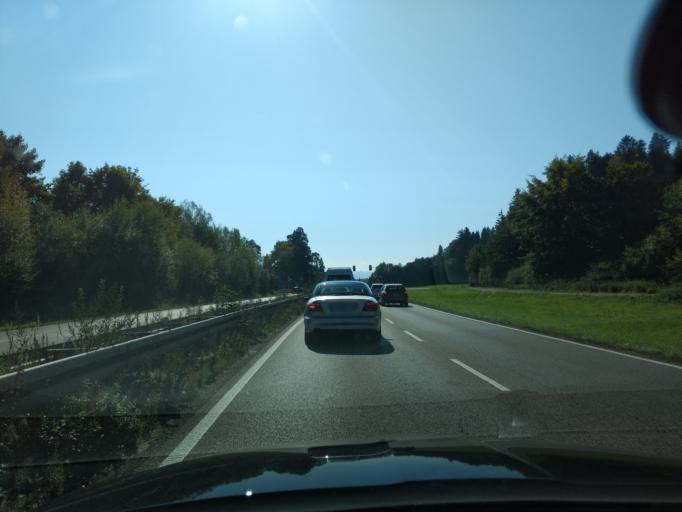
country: DE
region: Bavaria
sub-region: Upper Bavaria
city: Geretsried
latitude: 47.8837
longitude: 11.4566
